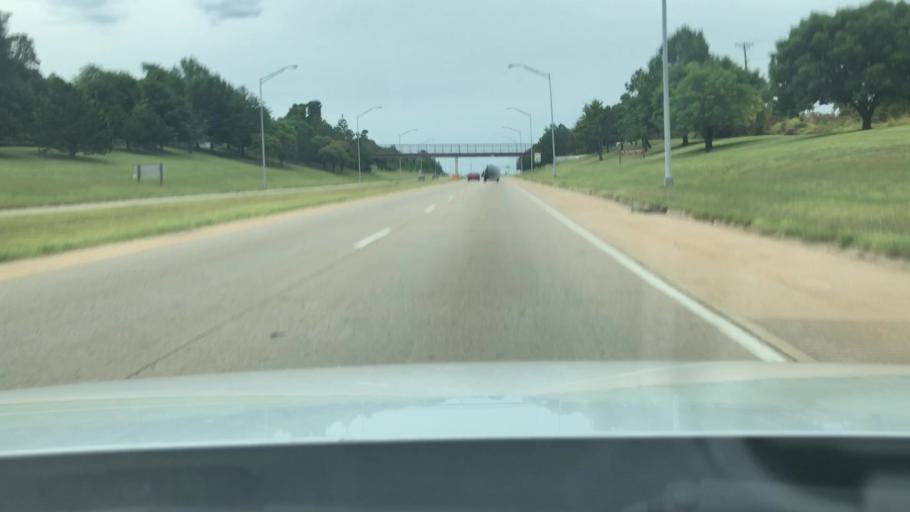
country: US
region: Oklahoma
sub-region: Tulsa County
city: Tulsa
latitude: 36.1711
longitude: -96.0008
